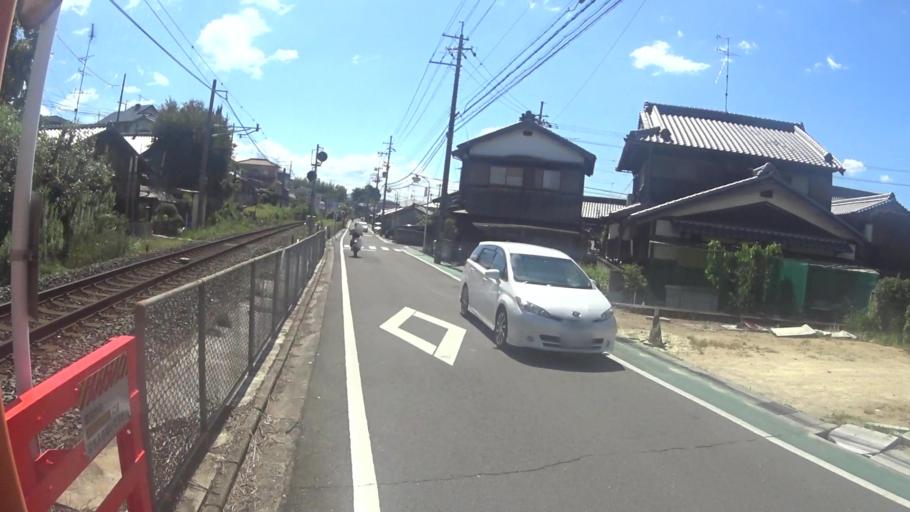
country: JP
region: Kyoto
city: Tanabe
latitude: 34.7940
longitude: 135.8094
